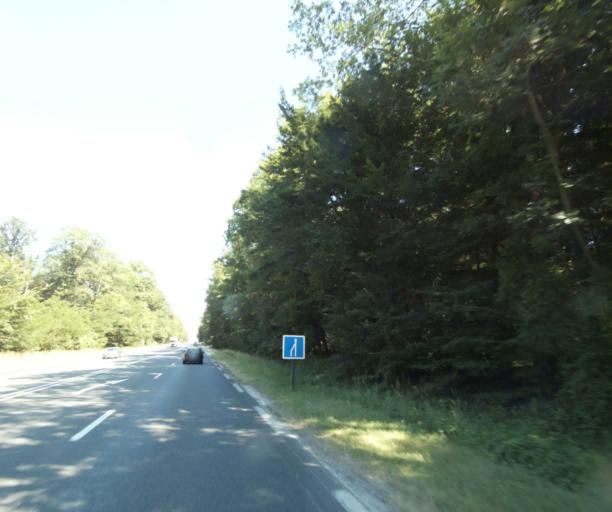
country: FR
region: Ile-de-France
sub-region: Departement de Seine-et-Marne
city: Veneux-les-Sablons
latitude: 48.3687
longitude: 2.7969
